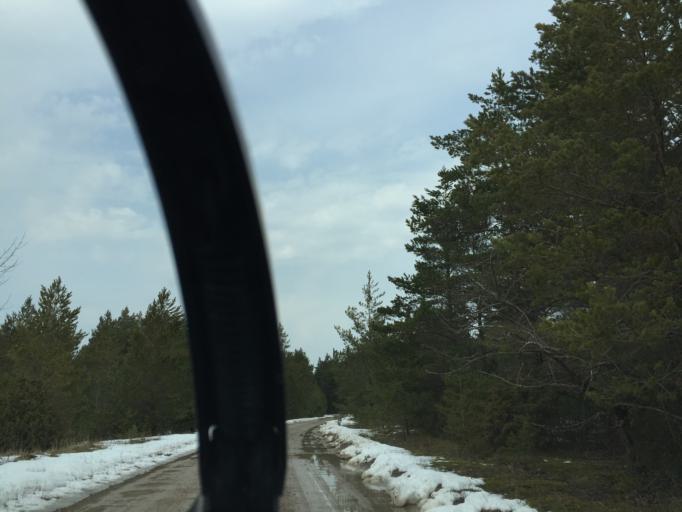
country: EE
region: Saare
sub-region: Kuressaare linn
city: Kuressaare
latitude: 58.4288
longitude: 22.1445
